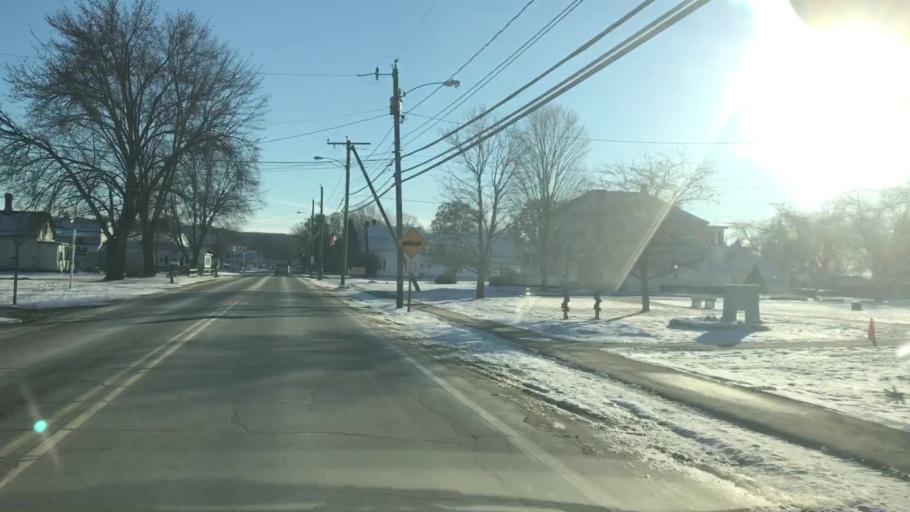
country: US
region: New Hampshire
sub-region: Grafton County
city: North Haverhill
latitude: 44.0936
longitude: -72.0255
